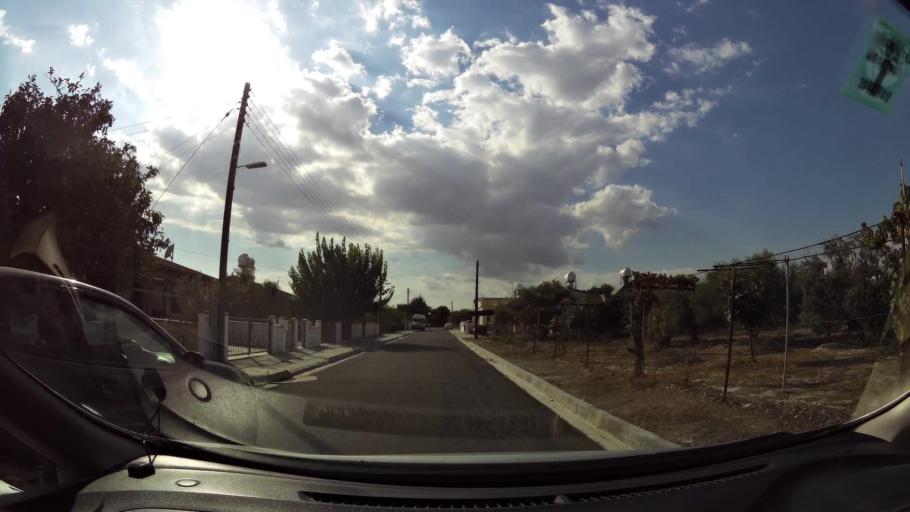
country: CY
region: Larnaka
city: Livadia
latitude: 34.9478
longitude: 33.6235
